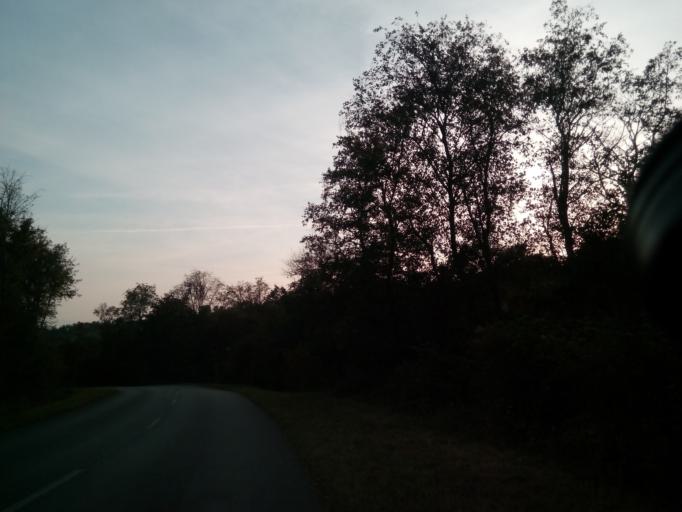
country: SK
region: Presovsky
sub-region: Okres Bardejov
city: Bardejov
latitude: 49.3467
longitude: 21.3384
